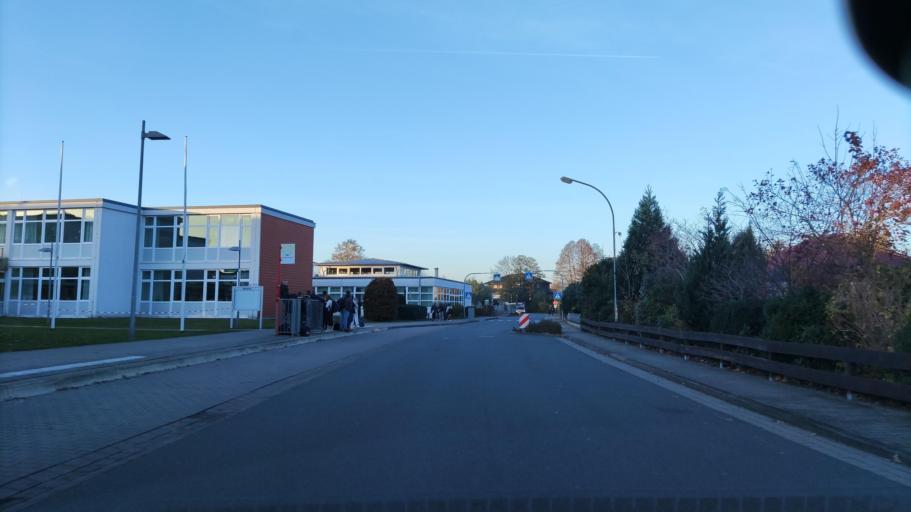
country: DE
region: Lower Saxony
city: Bleckede
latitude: 53.2857
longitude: 10.7312
